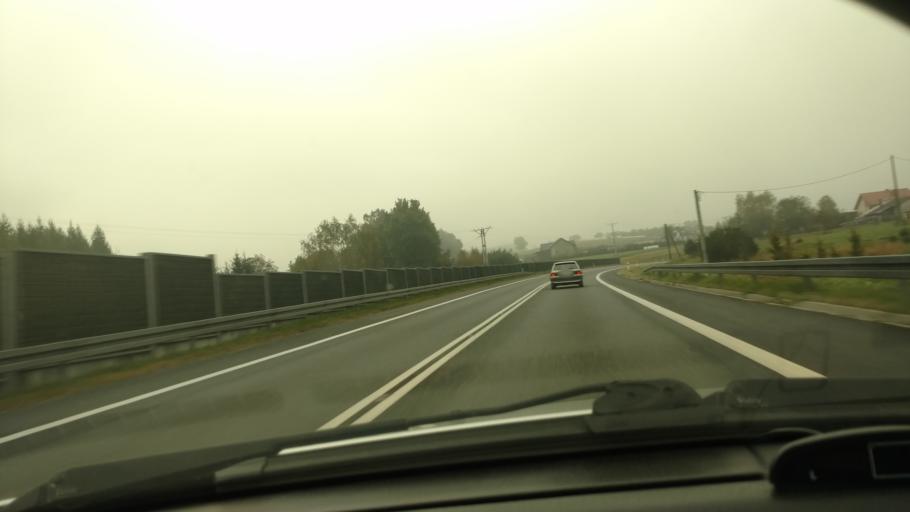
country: PL
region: Lesser Poland Voivodeship
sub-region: Powiat gorlicki
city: Biecz
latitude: 49.7167
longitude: 21.2511
